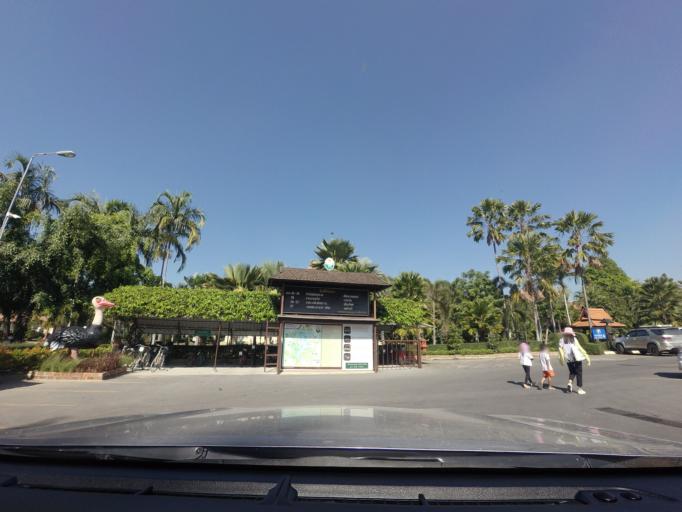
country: TH
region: Chiang Mai
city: San Sai
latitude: 18.8577
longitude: 99.0999
